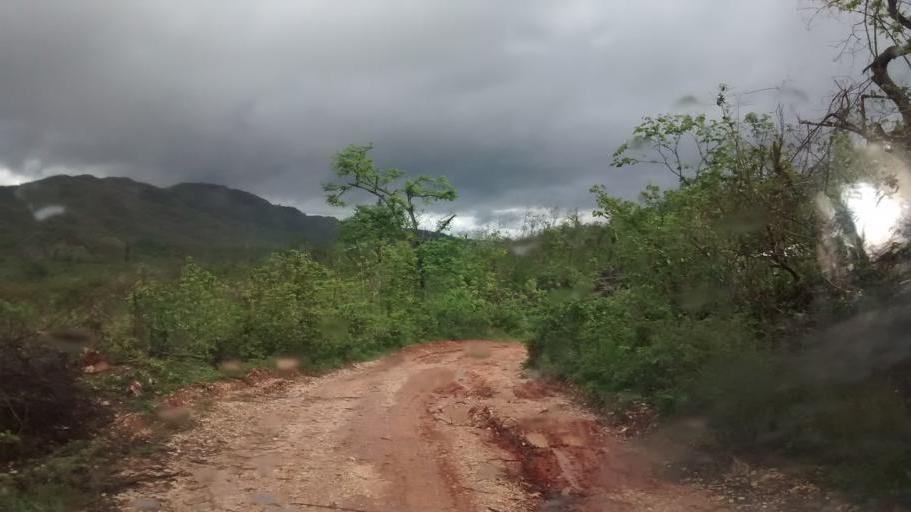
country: HT
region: Grandans
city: Corail
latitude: 18.5368
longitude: -73.9887
